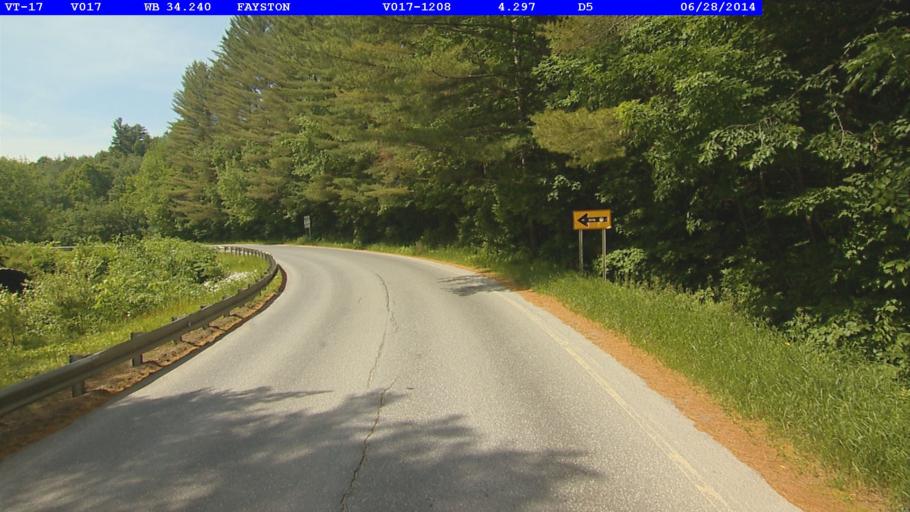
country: US
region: Vermont
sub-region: Washington County
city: Waterbury
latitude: 44.1850
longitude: -72.8713
